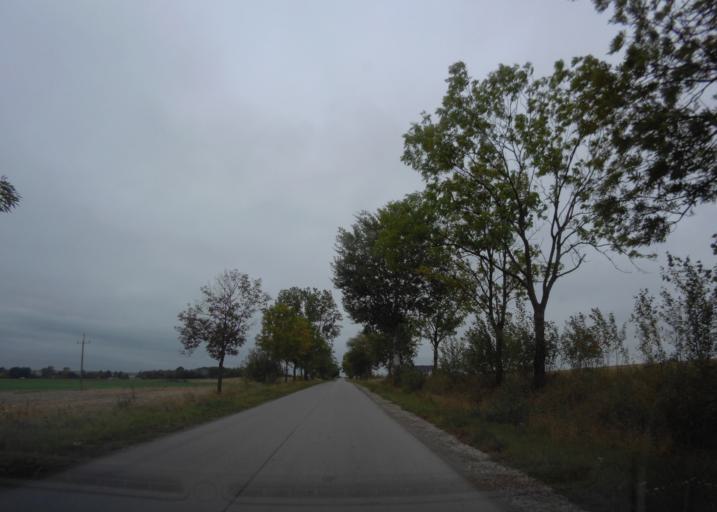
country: PL
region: Lublin Voivodeship
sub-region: Powiat chelmski
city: Sawin
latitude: 51.2139
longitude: 23.4401
